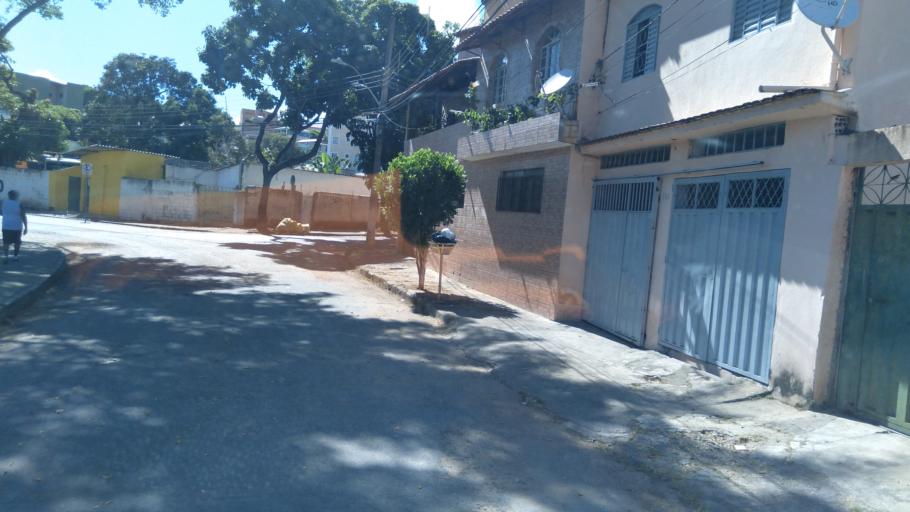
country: BR
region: Minas Gerais
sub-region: Belo Horizonte
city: Belo Horizonte
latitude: -19.8553
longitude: -43.9132
